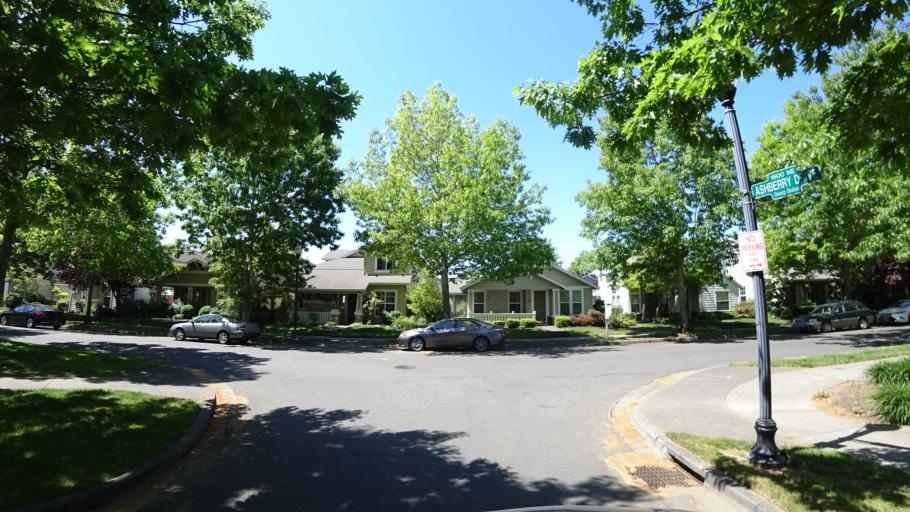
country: US
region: Oregon
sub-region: Washington County
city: Rockcreek
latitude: 45.5361
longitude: -122.9134
